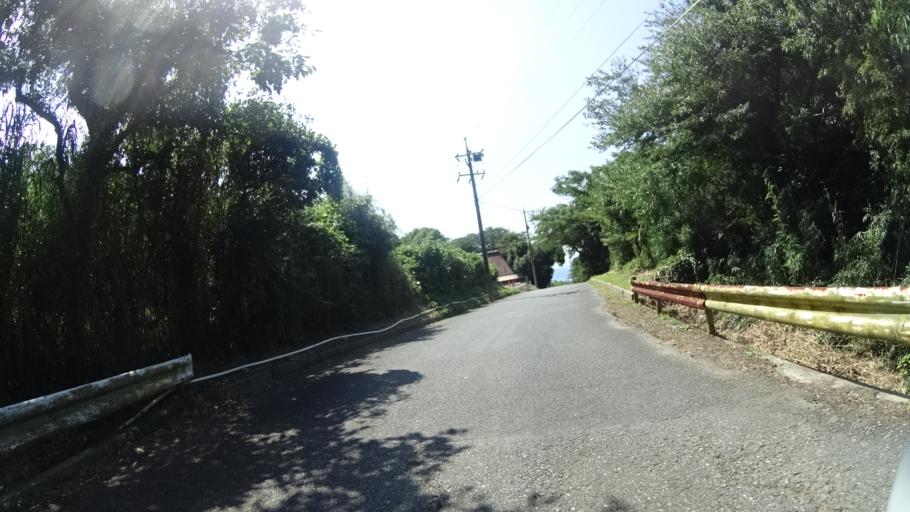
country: JP
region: Yamaguchi
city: Shimonoseki
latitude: 34.1052
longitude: 130.8690
